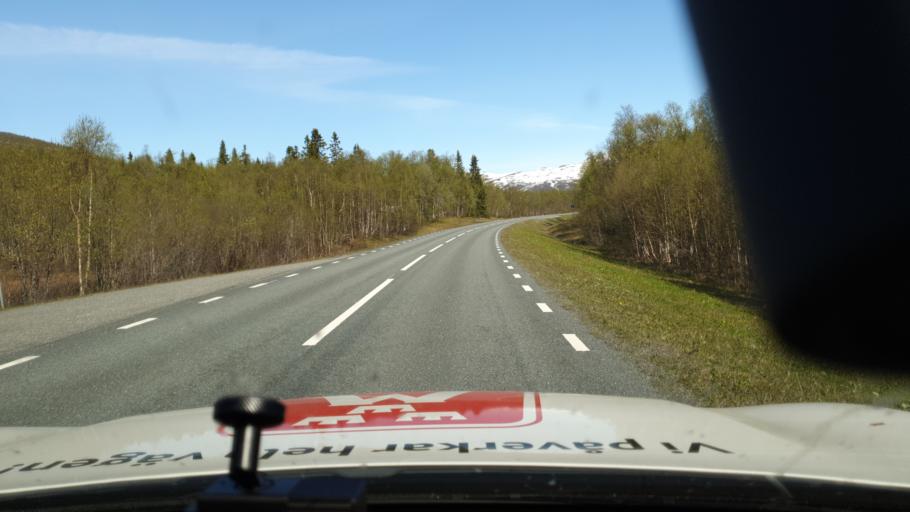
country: NO
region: Nordland
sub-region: Rana
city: Mo i Rana
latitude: 65.7692
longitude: 15.1122
